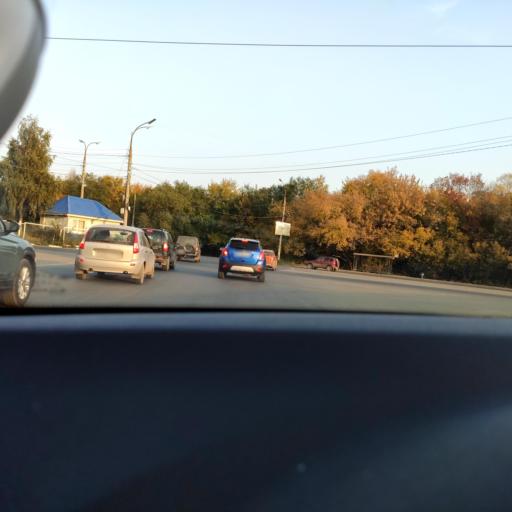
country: RU
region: Samara
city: Smyshlyayevka
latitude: 53.2512
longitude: 50.3590
